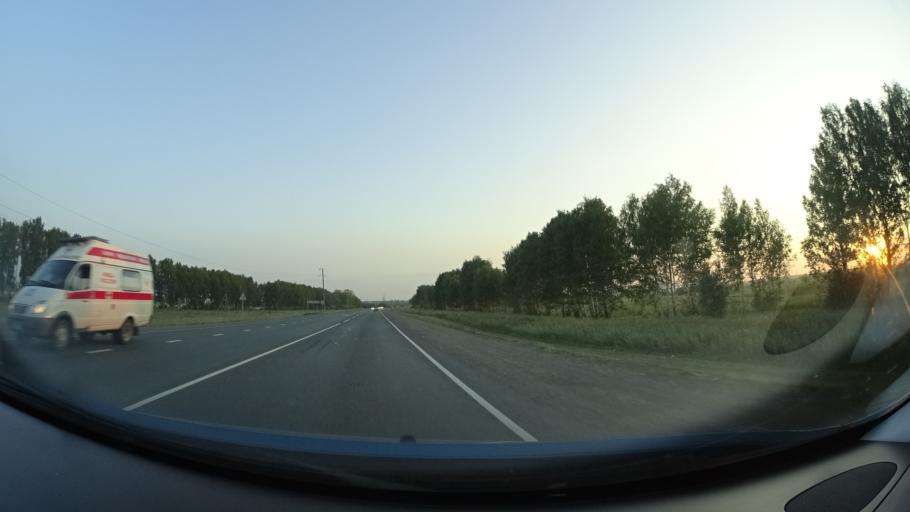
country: RU
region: Samara
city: Sernovodsk
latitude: 53.8936
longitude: 51.2647
